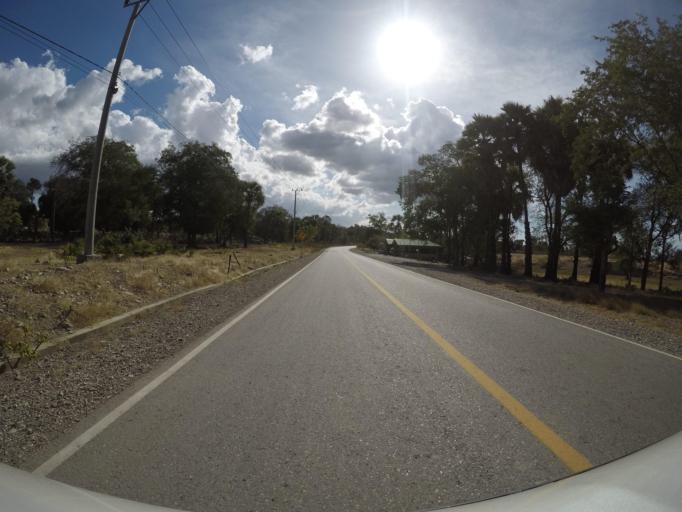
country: TL
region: Baucau
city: Baucau
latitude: -8.4840
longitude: 126.5542
